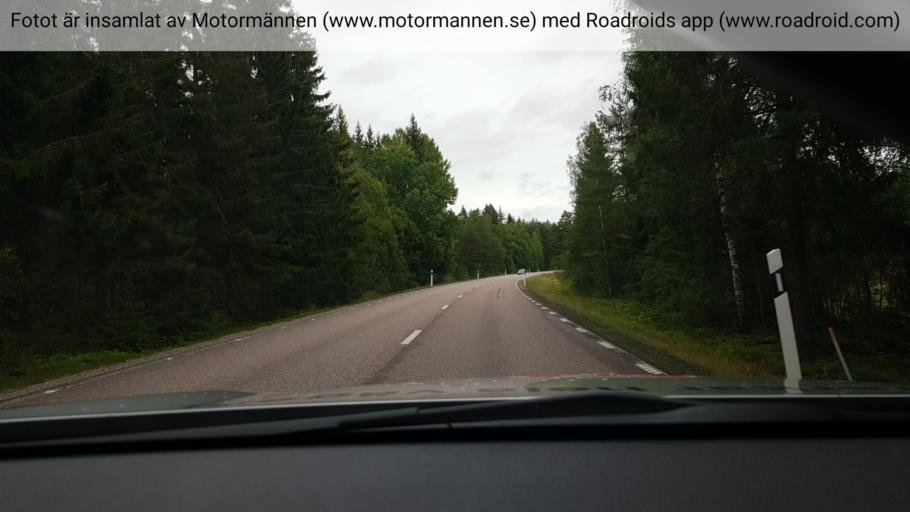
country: SE
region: Gaevleborg
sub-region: Gavle Kommun
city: Hedesunda
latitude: 60.3294
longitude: 16.9195
